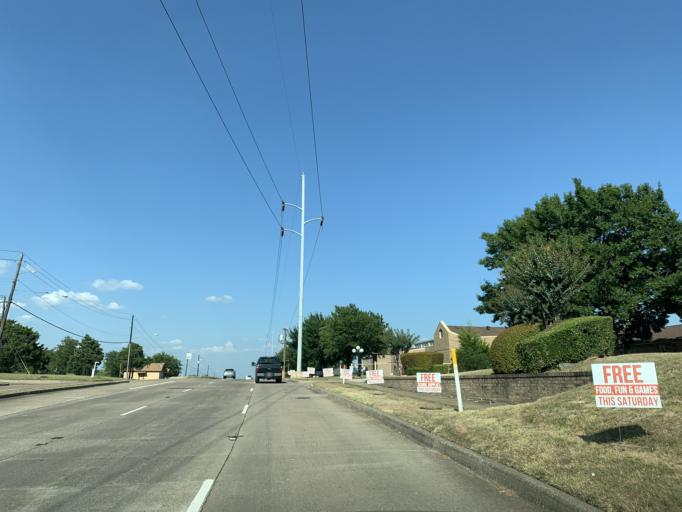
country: US
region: Texas
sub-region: Dallas County
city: Hutchins
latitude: 32.6628
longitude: -96.7833
